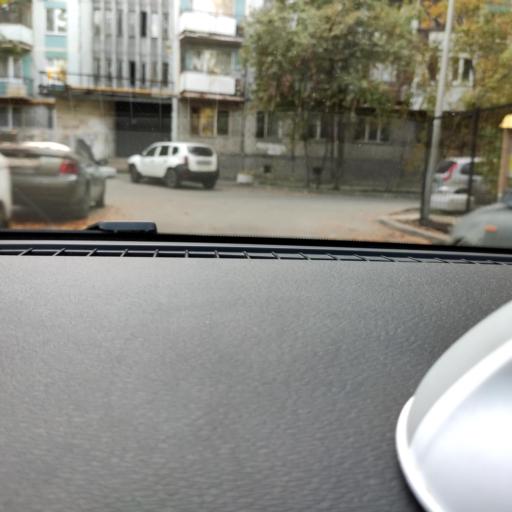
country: RU
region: Samara
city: Samara
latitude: 53.1981
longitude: 50.1361
